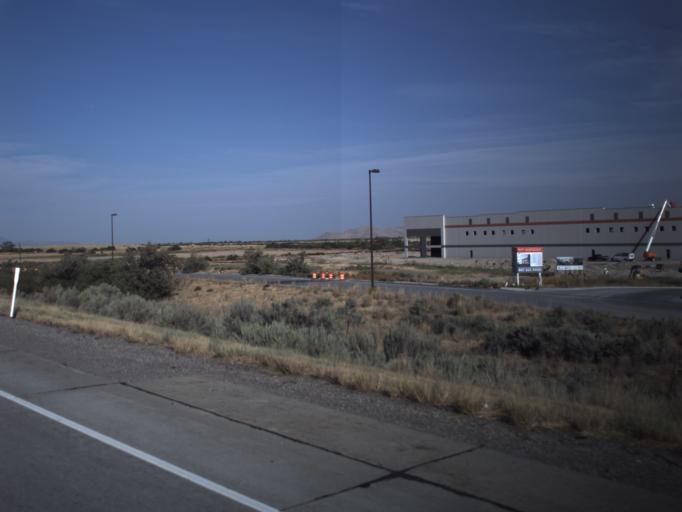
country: US
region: Utah
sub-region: Salt Lake County
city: West Valley City
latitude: 40.7712
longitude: -112.0356
